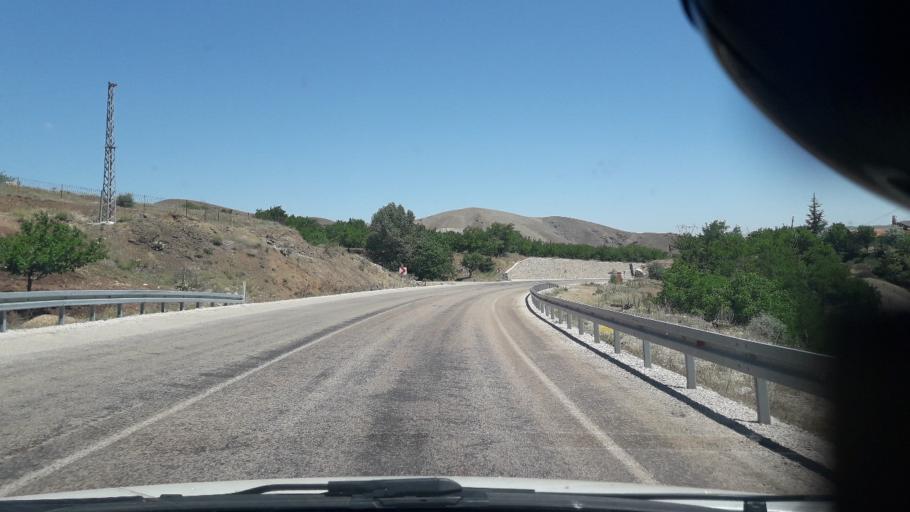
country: TR
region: Malatya
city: Hekimhan
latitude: 38.8399
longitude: 37.8415
